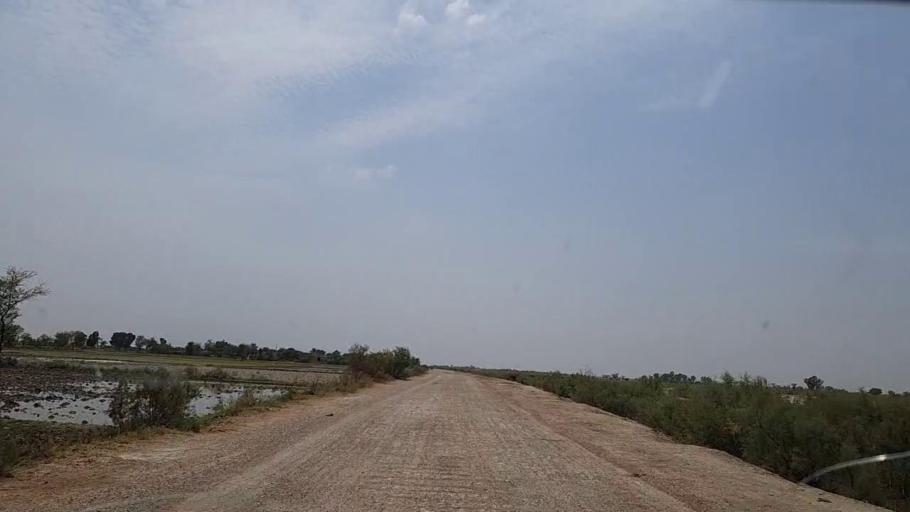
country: PK
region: Sindh
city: Phulji
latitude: 26.8811
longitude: 67.6734
